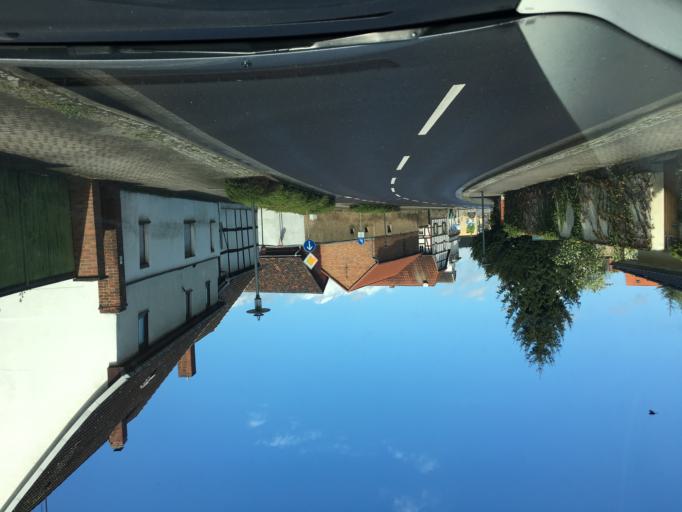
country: DE
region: Saxony-Anhalt
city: Haldensleben I
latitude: 52.2647
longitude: 11.4223
